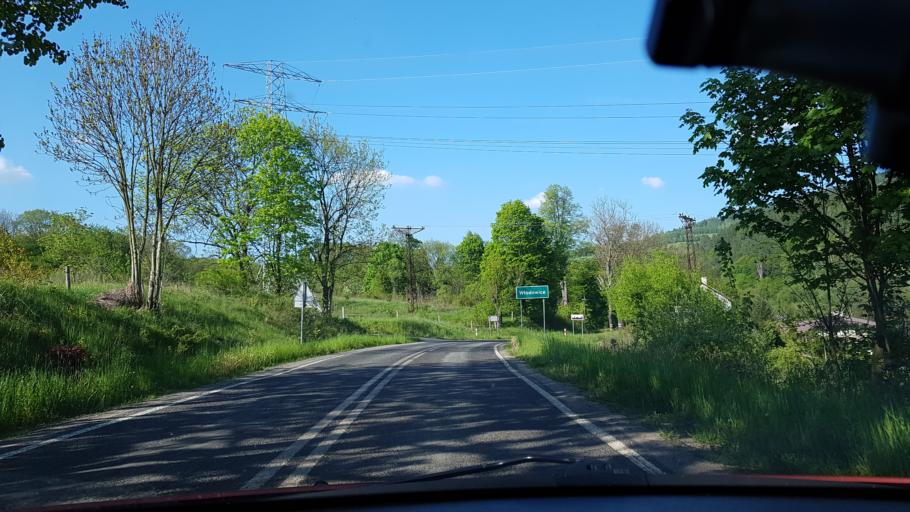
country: PL
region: Lower Silesian Voivodeship
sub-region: Powiat klodzki
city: Nowa Ruda
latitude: 50.5614
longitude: 16.4678
